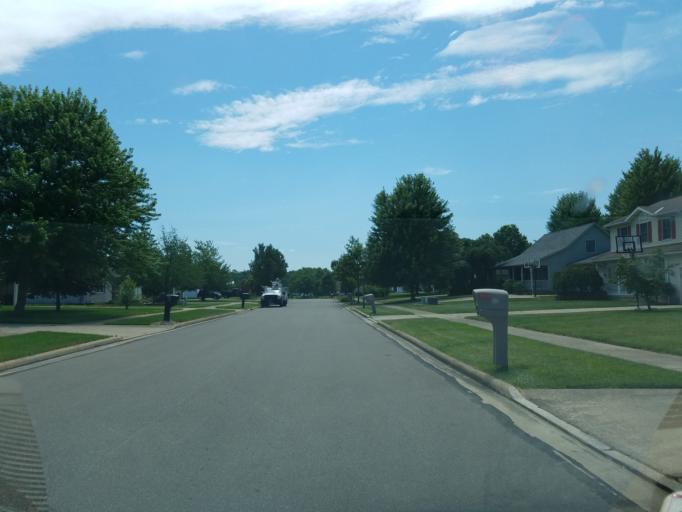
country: US
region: Ohio
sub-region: Ashland County
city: Ashland
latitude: 40.8693
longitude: -82.3389
